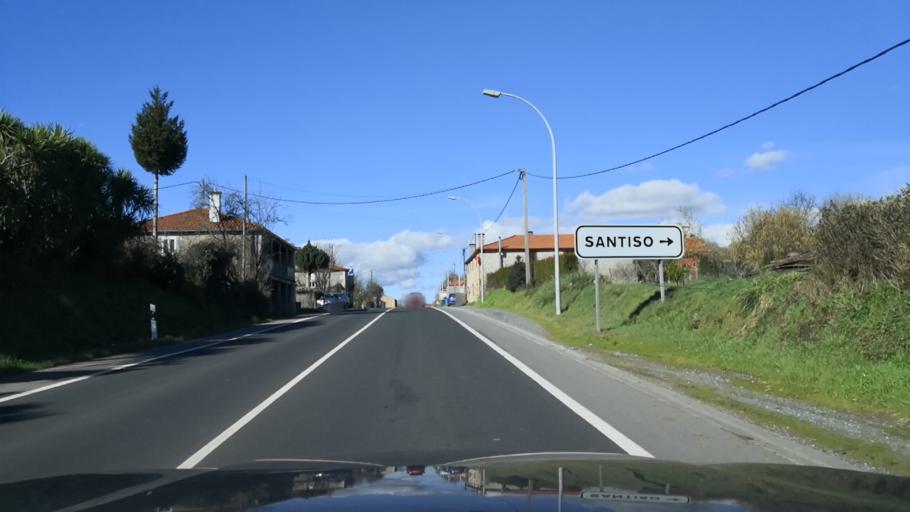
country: ES
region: Galicia
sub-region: Provincia de Pontevedra
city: Lalin
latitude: 42.6778
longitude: -8.1655
